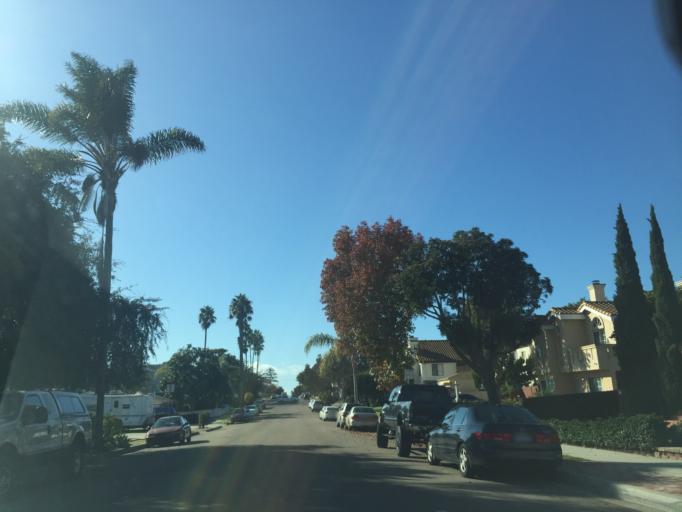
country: US
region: California
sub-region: San Diego County
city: La Jolla
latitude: 32.7973
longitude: -117.2385
